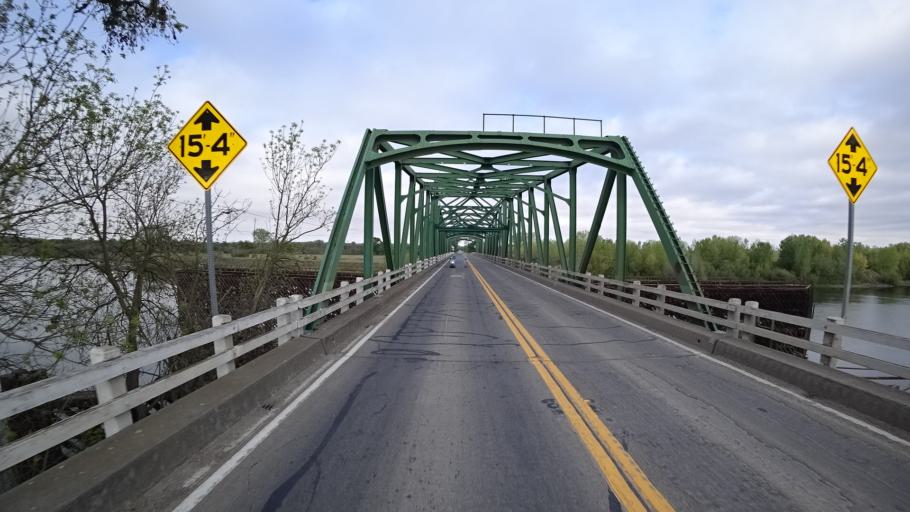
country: US
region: California
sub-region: Glenn County
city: Willows
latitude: 39.4574
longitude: -121.9943
